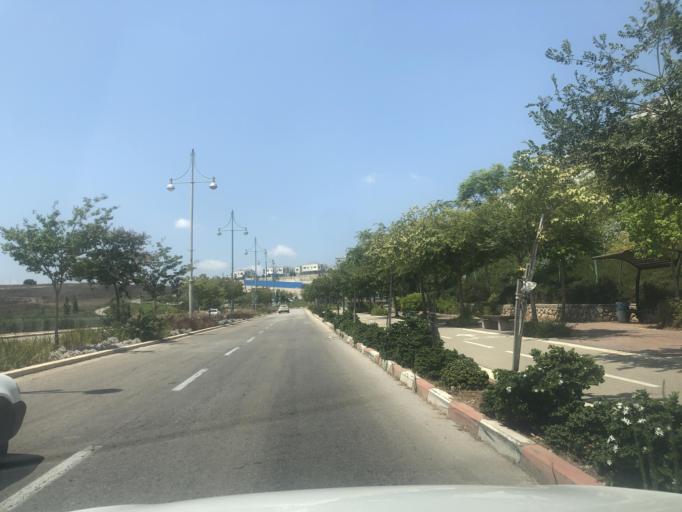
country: IL
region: Haifa
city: Daliyat el Karmil
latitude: 32.6360
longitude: 35.0834
